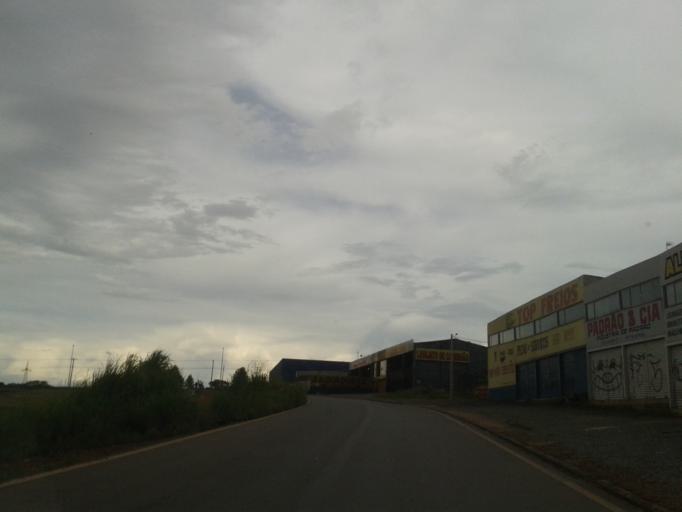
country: BR
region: Goias
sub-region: Aparecida De Goiania
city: Aparecida de Goiania
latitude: -16.7879
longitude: -49.2399
